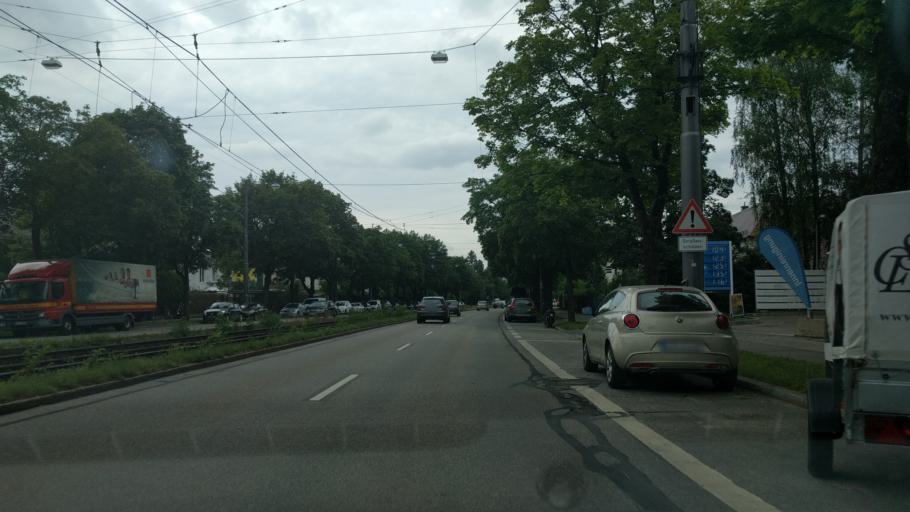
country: DE
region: Bavaria
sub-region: Upper Bavaria
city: Munich
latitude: 48.0965
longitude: 11.5639
